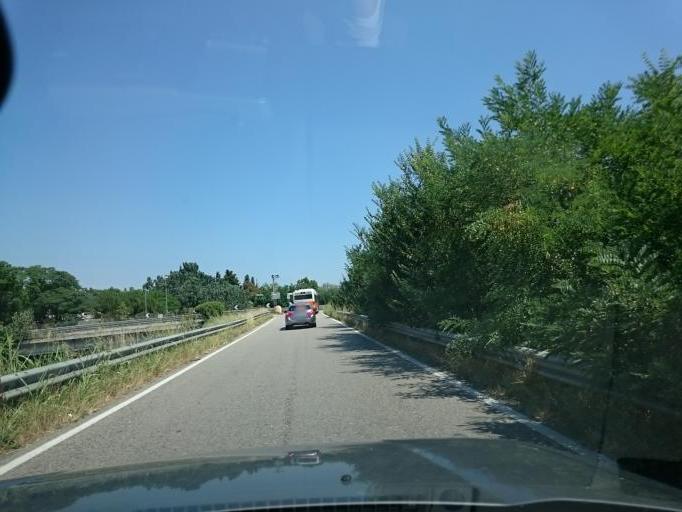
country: IT
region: Veneto
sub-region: Provincia di Padova
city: Mandriola-Sant'Agostino
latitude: 45.3981
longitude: 11.8441
